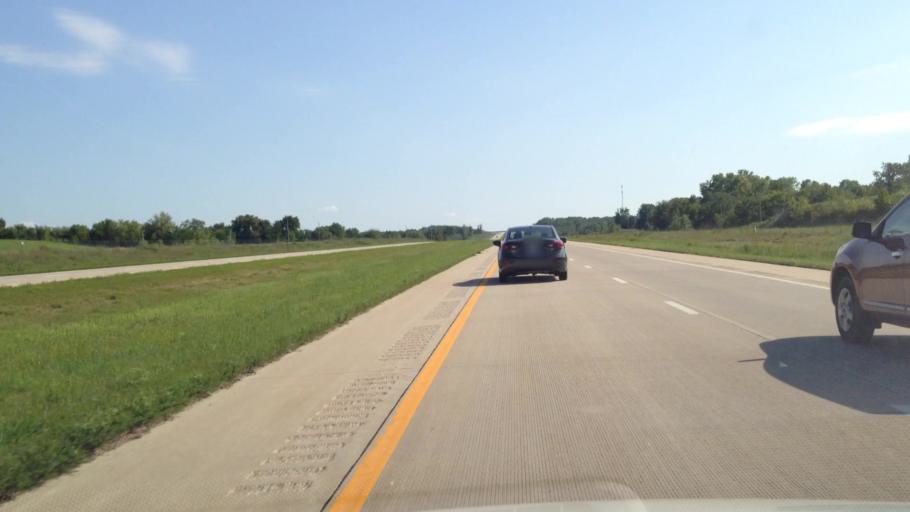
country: US
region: Kansas
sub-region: Linn County
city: Pleasanton
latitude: 38.1295
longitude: -94.7120
